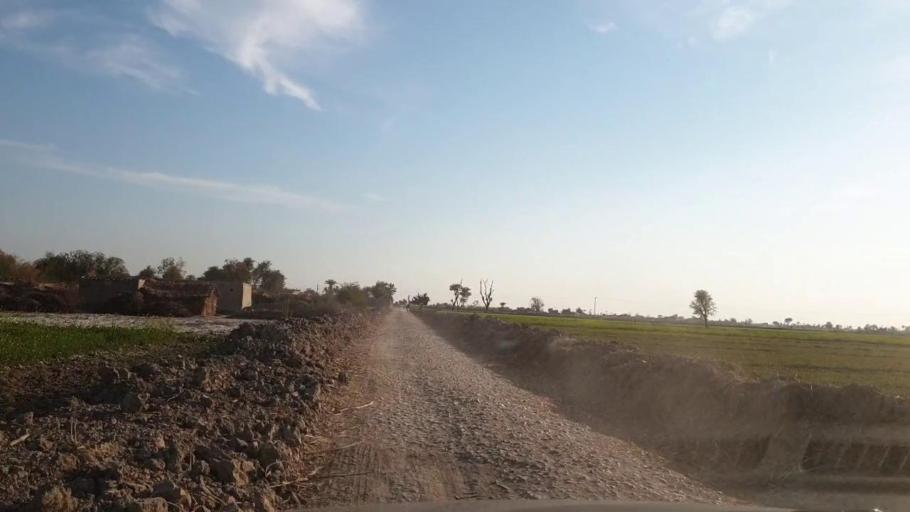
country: PK
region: Sindh
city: Khadro
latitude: 26.1732
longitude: 68.7529
